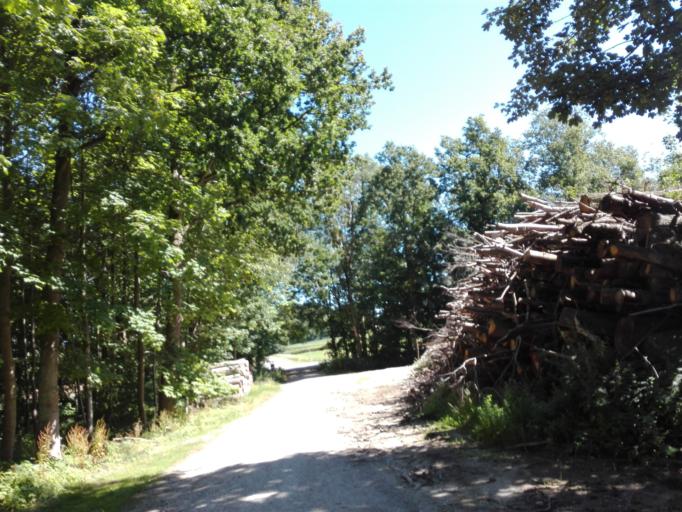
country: DK
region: Central Jutland
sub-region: Odder Kommune
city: Odder
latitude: 55.9498
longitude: 10.1505
